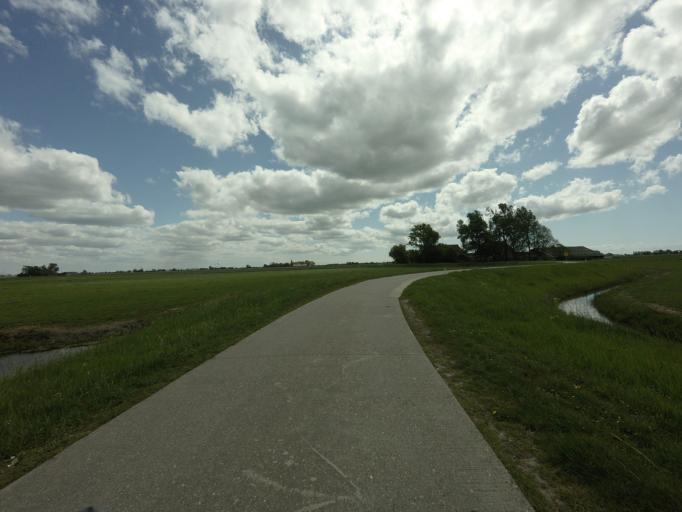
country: NL
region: Friesland
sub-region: Gemeente Littenseradiel
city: Wommels
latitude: 53.1205
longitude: 5.5532
